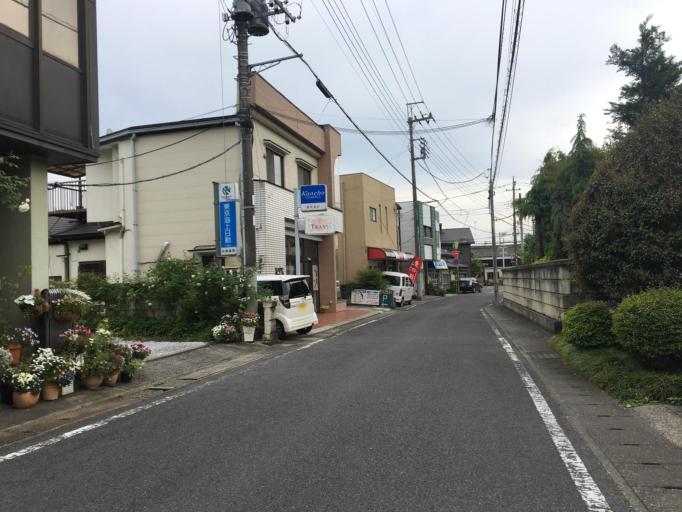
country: JP
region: Tochigi
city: Tochigi
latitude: 36.3940
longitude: 139.7356
